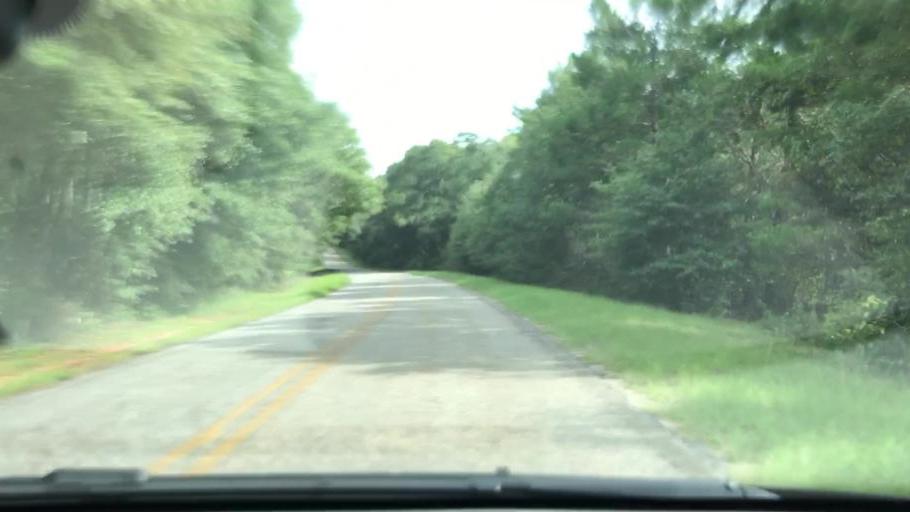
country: US
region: Georgia
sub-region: Early County
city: Blakely
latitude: 31.5090
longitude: -84.9510
